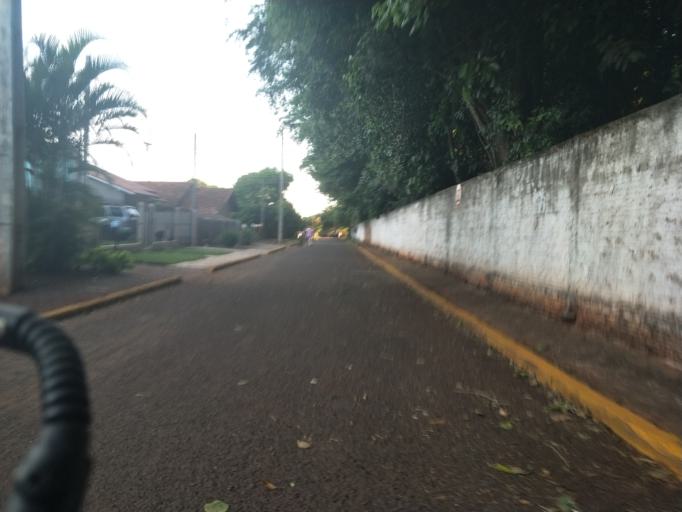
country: BR
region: Parana
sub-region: Marechal Candido Rondon
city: Marechal Candido Rondon
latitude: -24.5511
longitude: -54.0471
